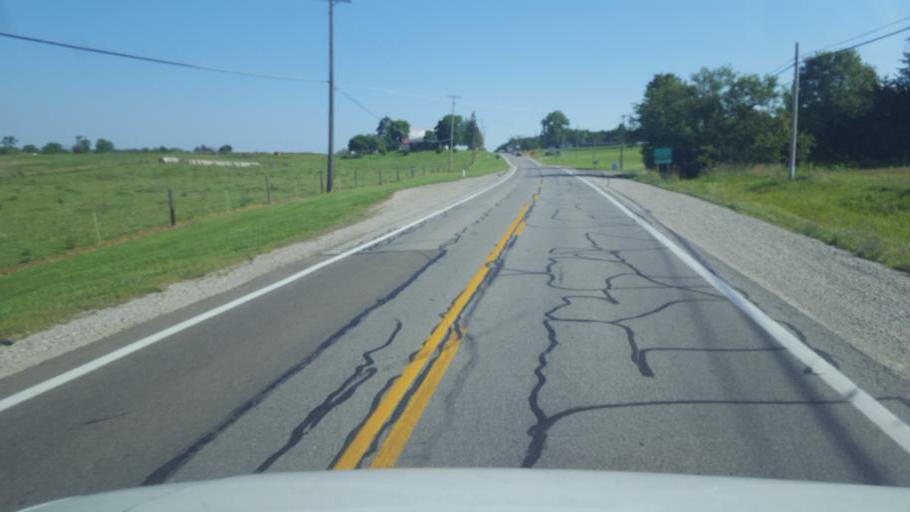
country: US
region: Ohio
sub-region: Morrow County
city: Mount Gilead
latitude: 40.5629
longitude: -82.8250
